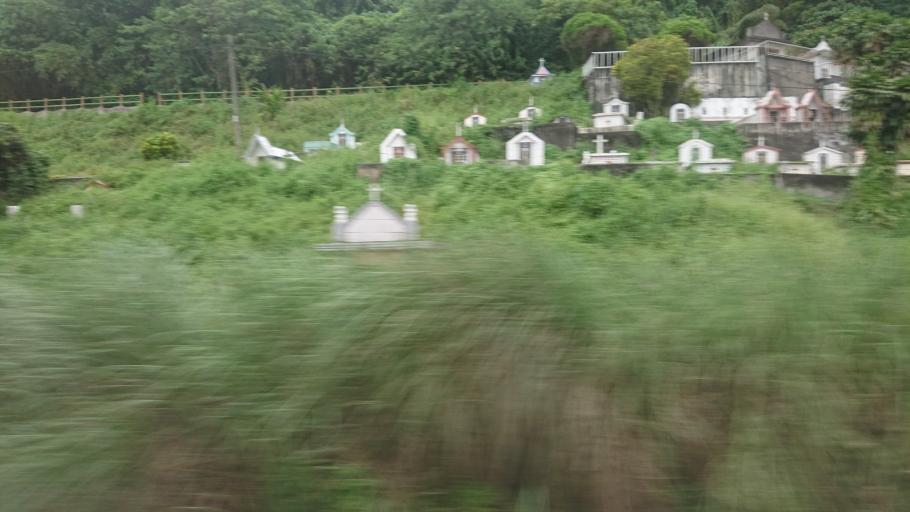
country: TW
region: Taiwan
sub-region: Hualien
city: Hualian
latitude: 23.5863
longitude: 121.3819
